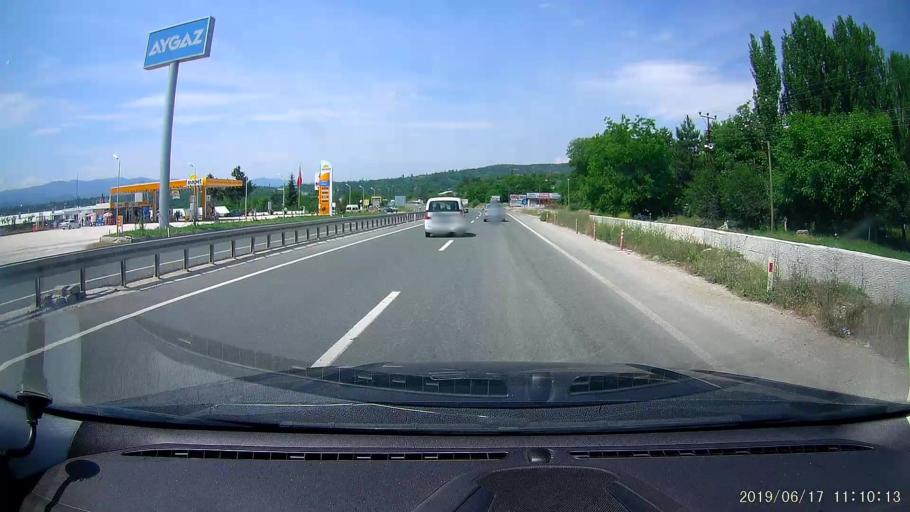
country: TR
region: Kastamonu
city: Tosya
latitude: 41.0010
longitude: 34.0279
